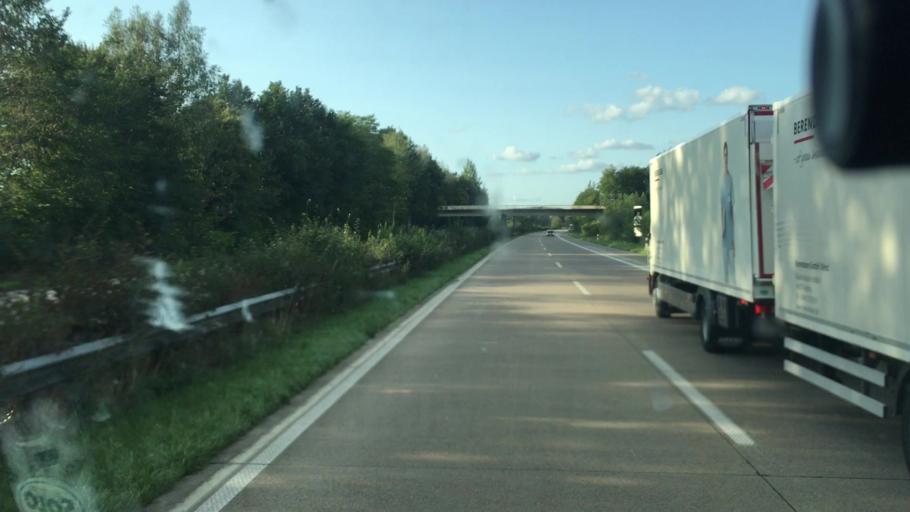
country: DE
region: Lower Saxony
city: Wiefelstede
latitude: 53.2878
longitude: 8.1501
